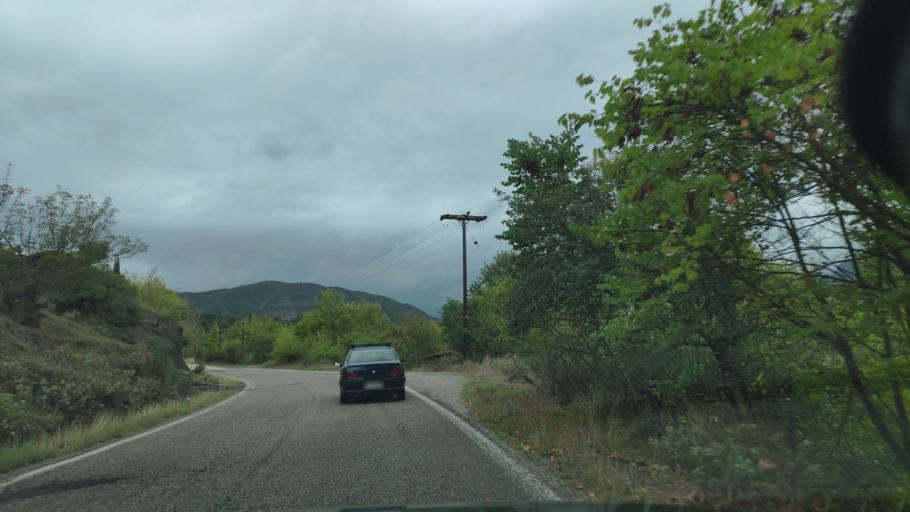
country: GR
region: West Greece
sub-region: Nomos Aitolias kai Akarnanias
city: Krikellos
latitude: 38.9607
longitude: 21.3335
